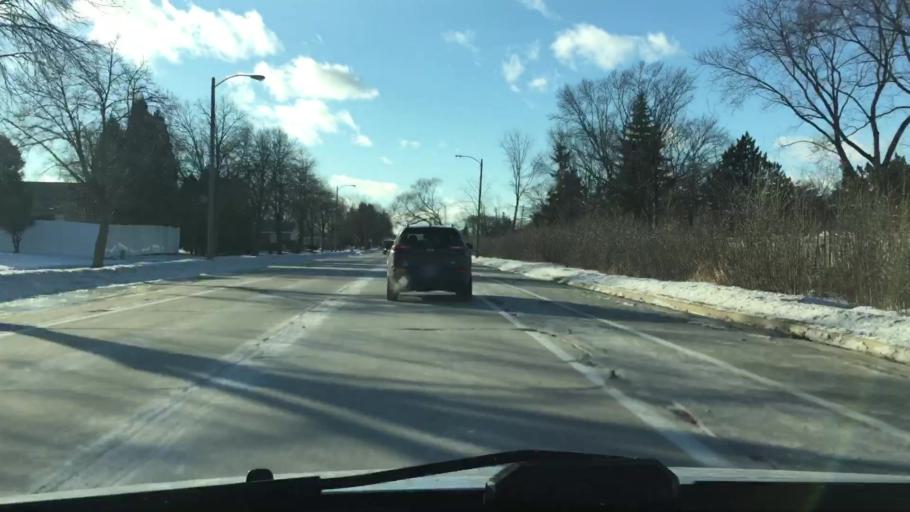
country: US
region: Wisconsin
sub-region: Milwaukee County
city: Greenfield
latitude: 42.9738
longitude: -88.0016
